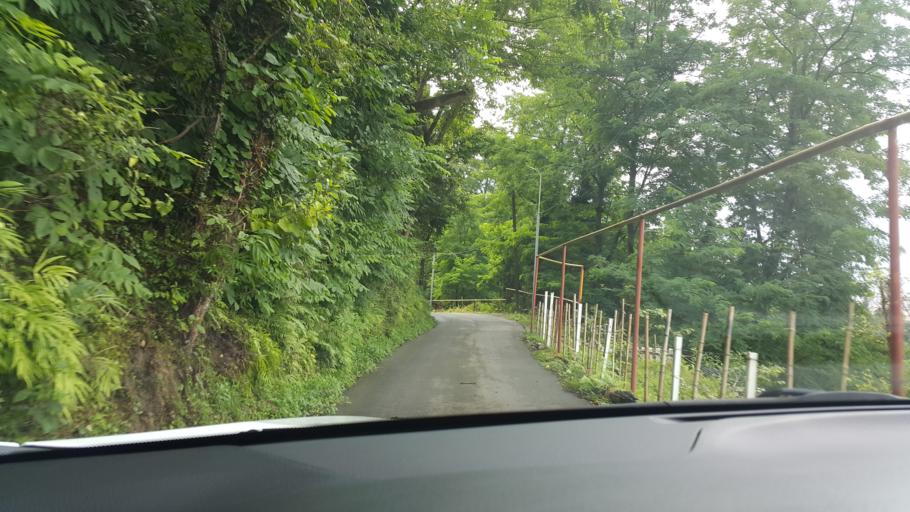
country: GE
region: Ajaria
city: Batumi
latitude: 41.6138
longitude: 41.6429
